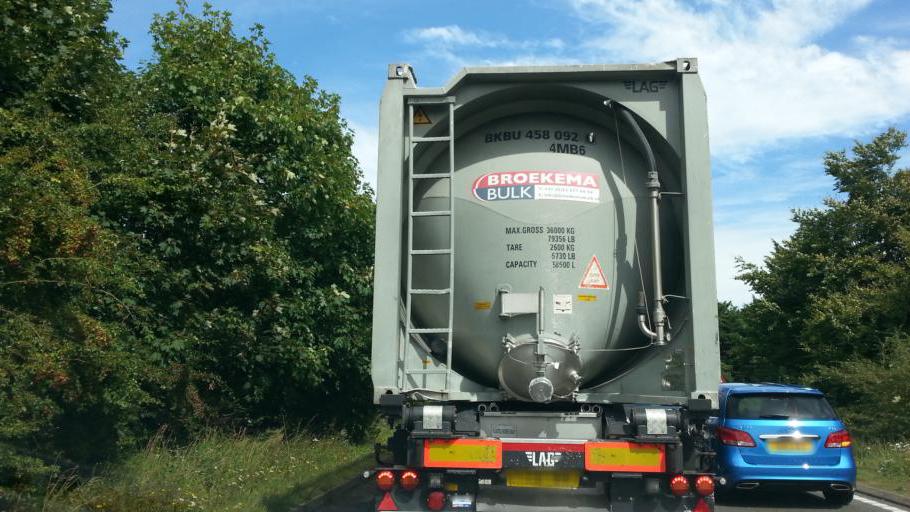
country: GB
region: England
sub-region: Suffolk
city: Exning
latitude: 52.2682
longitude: 0.3916
